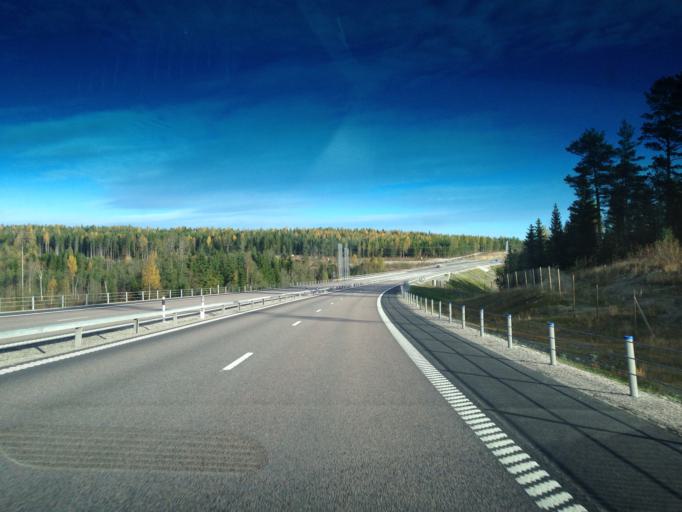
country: SE
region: Vaesternorrland
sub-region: Sundsvalls Kommun
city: Stockvik
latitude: 62.3316
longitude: 17.3454
